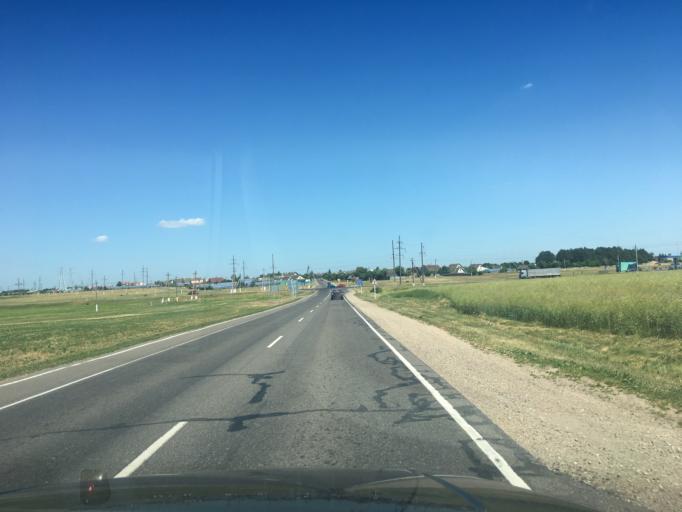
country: BY
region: Grodnenskaya
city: Iwye
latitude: 53.9132
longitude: 25.7646
